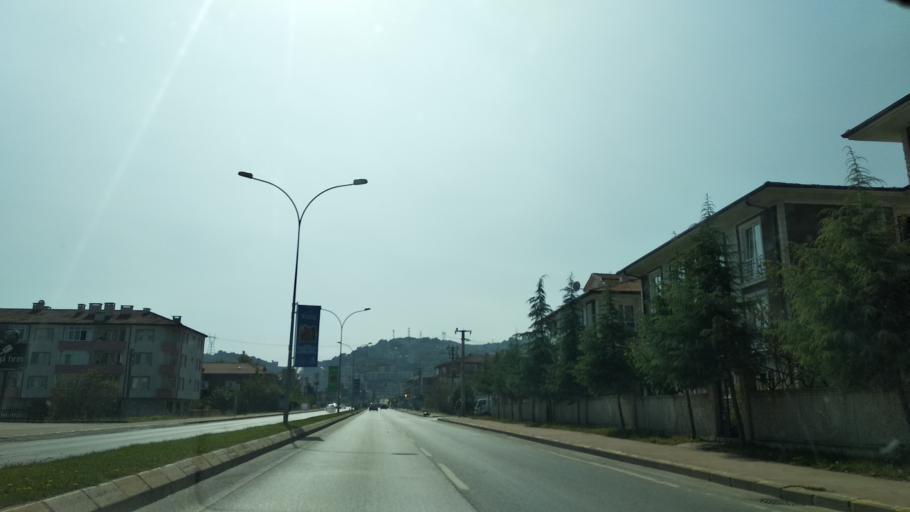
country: TR
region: Sakarya
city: Adapazari
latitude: 40.7643
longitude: 30.3634
